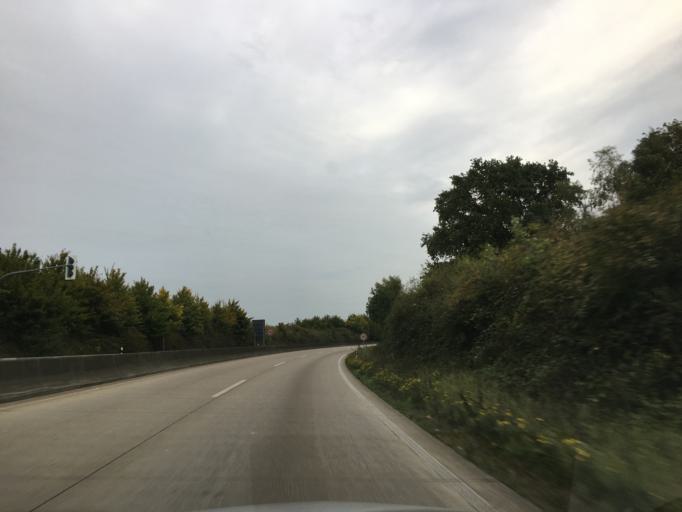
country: DE
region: North Rhine-Westphalia
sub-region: Regierungsbezirk Dusseldorf
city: Dusseldorf
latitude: 51.2867
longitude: 6.7419
